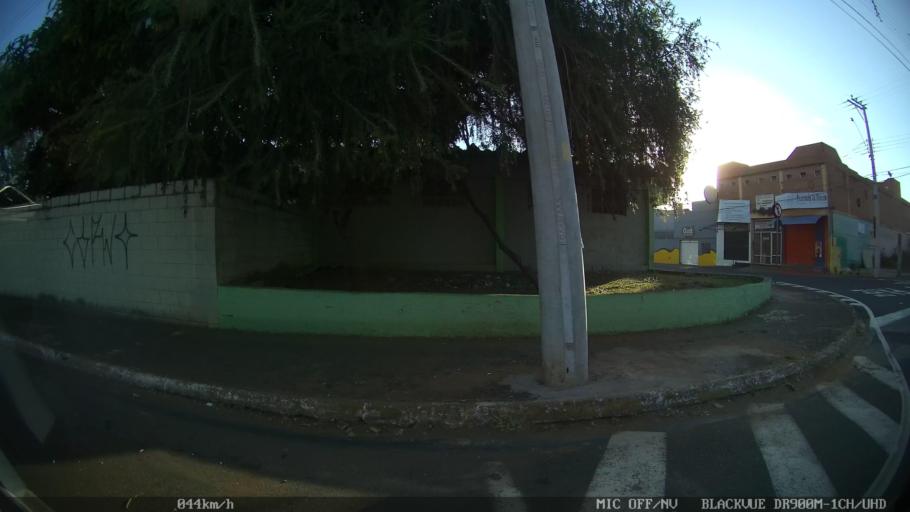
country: BR
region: Sao Paulo
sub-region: Franca
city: Franca
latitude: -20.5190
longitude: -47.3952
